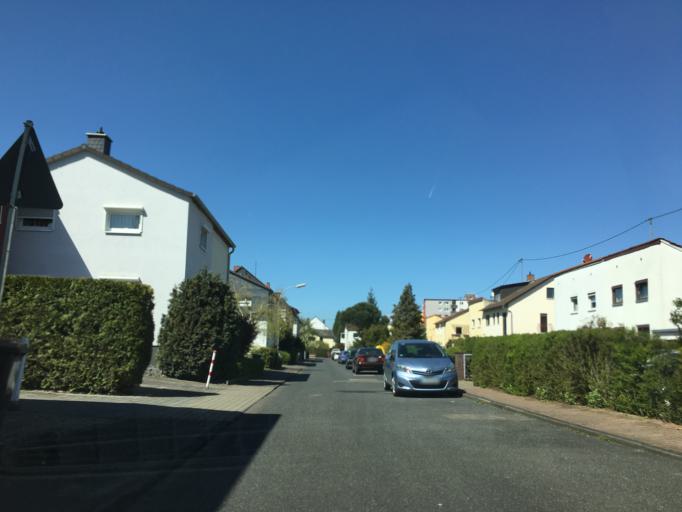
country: DE
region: Hesse
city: Niederrad
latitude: 50.0829
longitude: 8.5962
